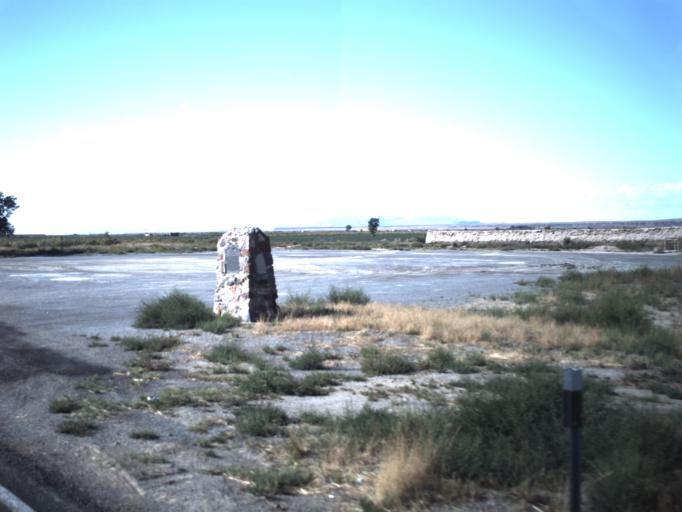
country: US
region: Utah
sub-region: Millard County
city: Delta
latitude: 39.2653
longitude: -112.6532
